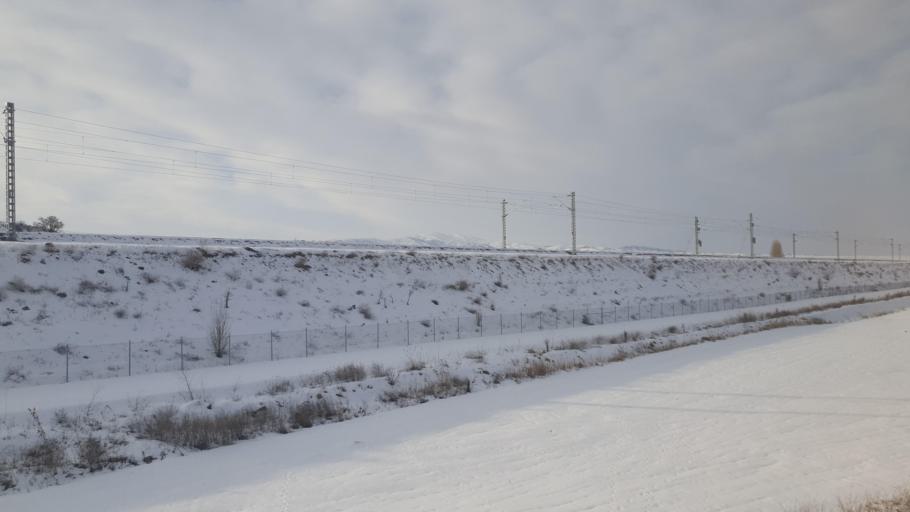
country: TR
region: Kirikkale
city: Baliseyh
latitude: 39.9270
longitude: 33.7862
